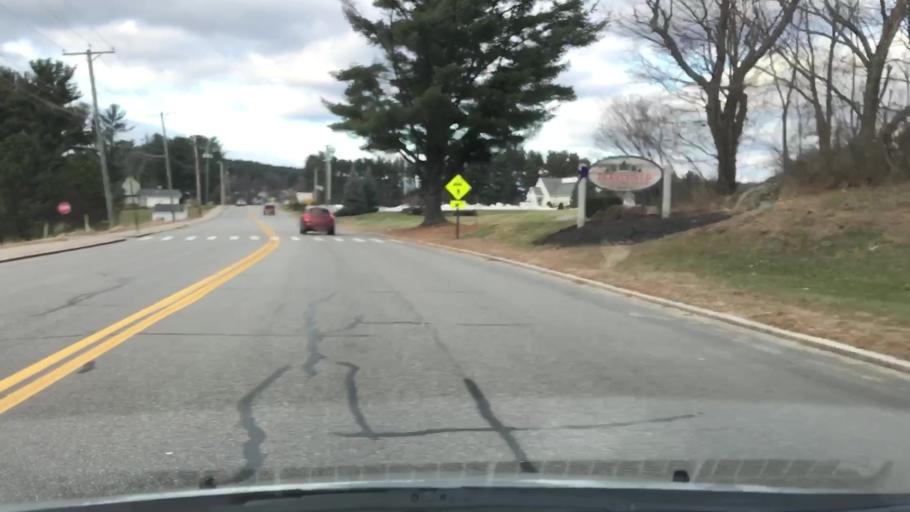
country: US
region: New Hampshire
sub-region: Hillsborough County
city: Manchester
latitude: 42.9913
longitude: -71.4337
